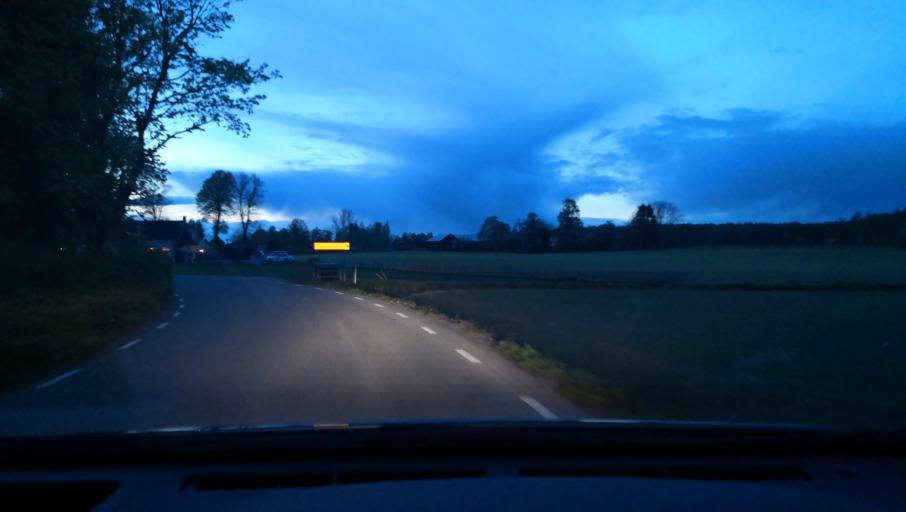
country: SE
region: OErebro
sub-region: Orebro Kommun
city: Vintrosa
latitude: 59.1512
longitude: 15.0059
